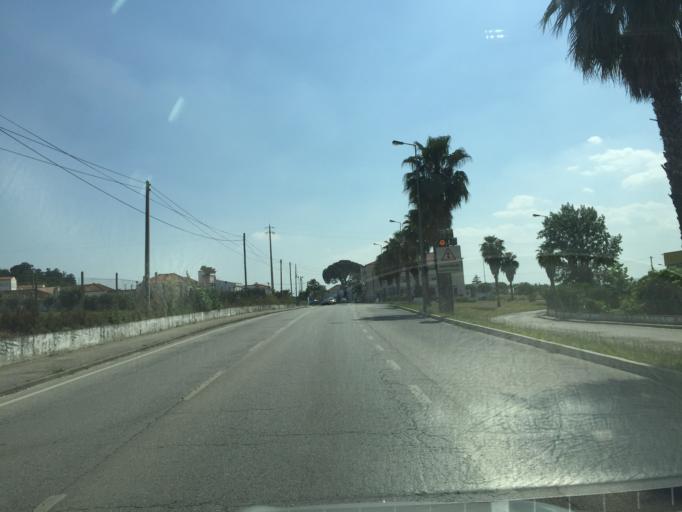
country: PT
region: Santarem
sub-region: Golega
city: Golega
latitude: 39.3663
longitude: -8.4751
